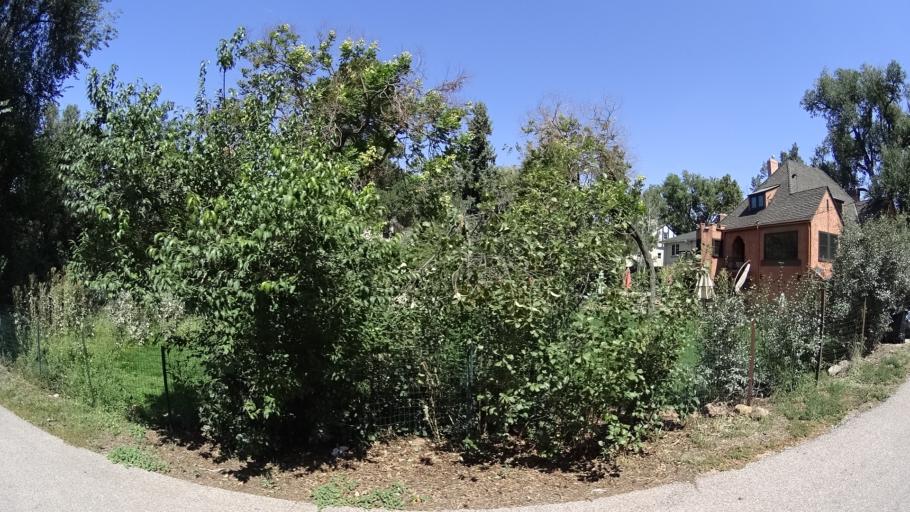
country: US
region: Colorado
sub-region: El Paso County
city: Colorado Springs
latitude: 38.8645
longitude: -104.8261
